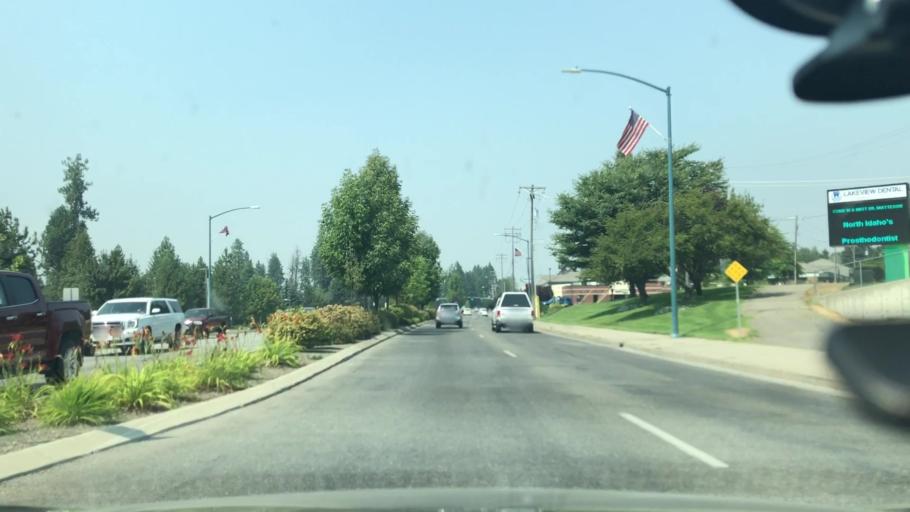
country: US
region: Idaho
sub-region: Kootenai County
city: Coeur d'Alene
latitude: 47.6801
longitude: -116.7916
